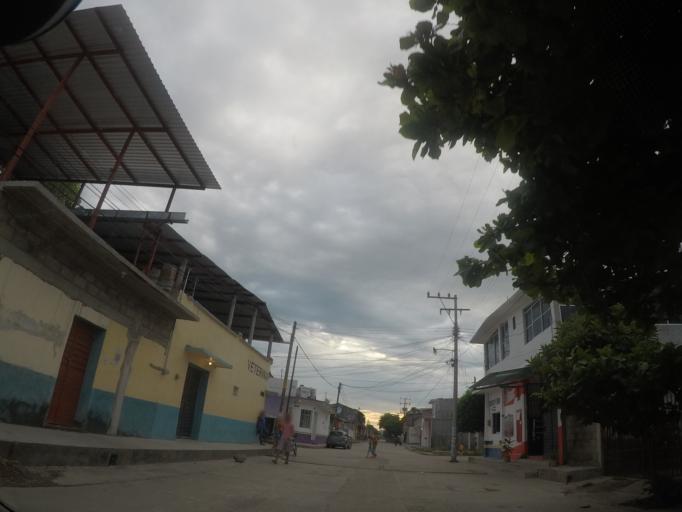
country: MX
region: Oaxaca
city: Chahuite
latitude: 16.2882
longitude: -94.1946
